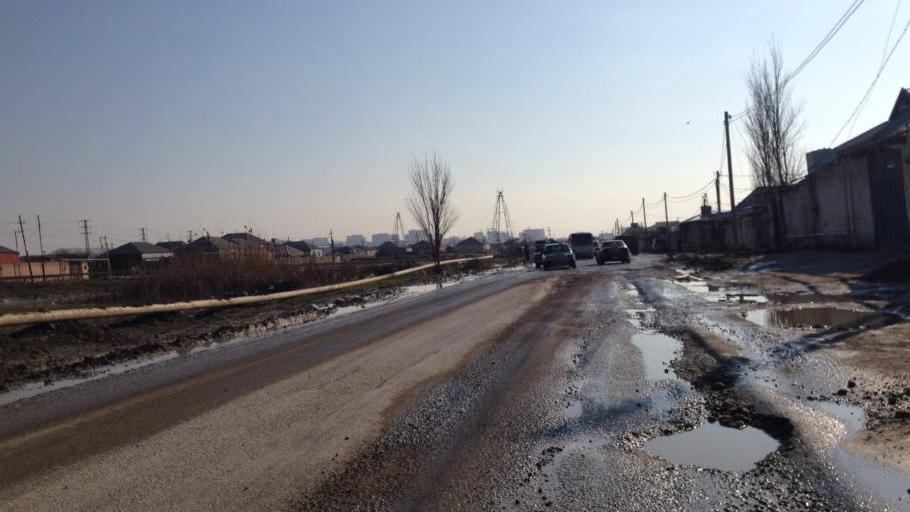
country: AZ
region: Baki
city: Balakhani
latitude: 40.4515
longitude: 49.9316
